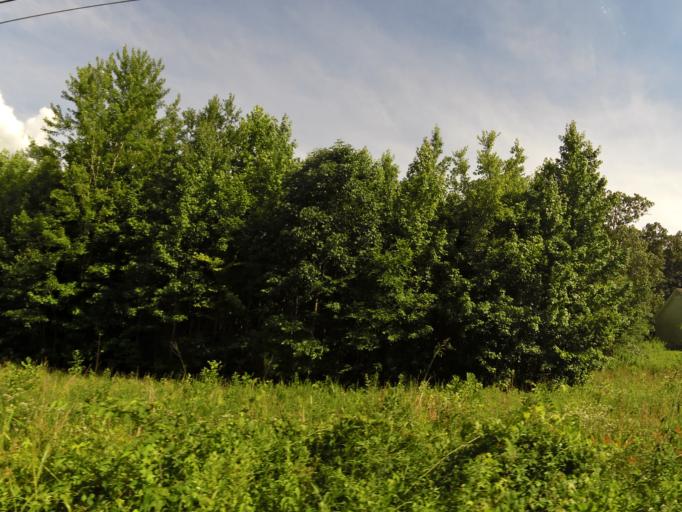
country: US
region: Tennessee
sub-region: Carroll County
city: Huntingdon
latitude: 36.0189
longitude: -88.3876
